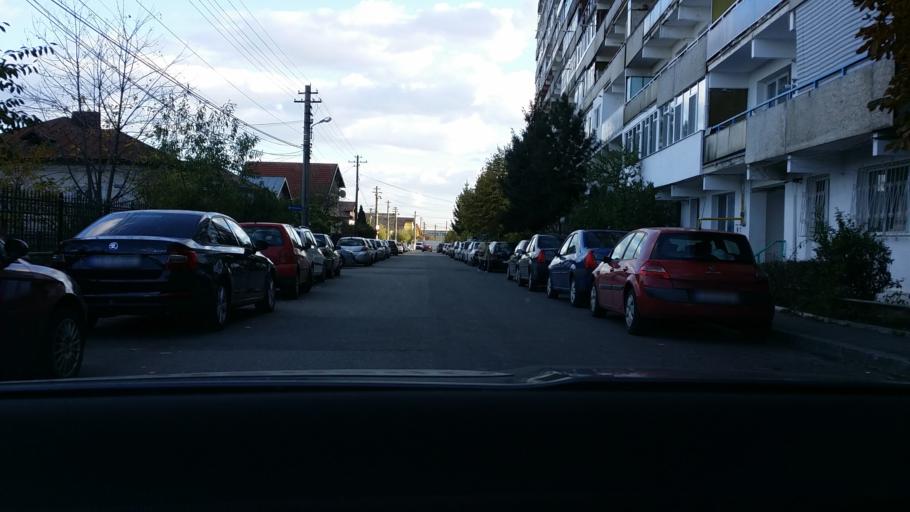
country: RO
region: Prahova
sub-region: Municipiul Campina
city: Campina
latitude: 45.1275
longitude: 25.7428
